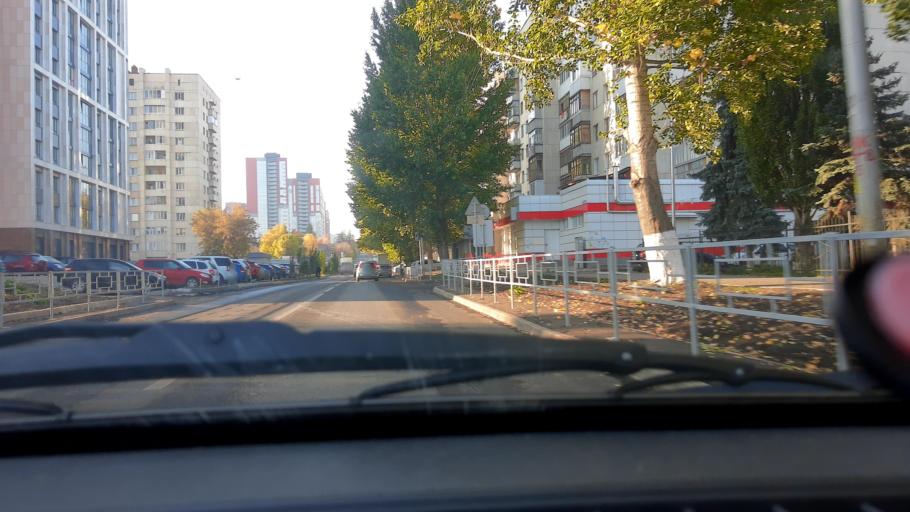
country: RU
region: Bashkortostan
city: Ufa
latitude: 54.7361
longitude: 55.9329
